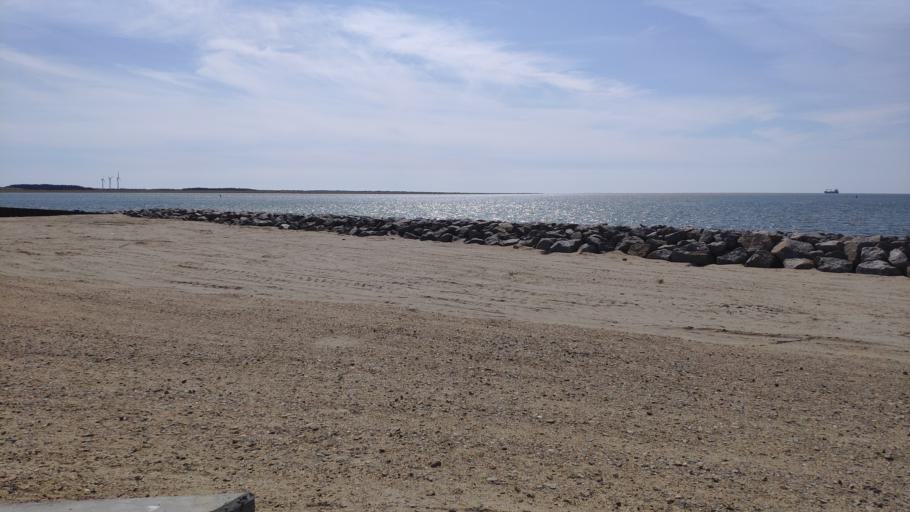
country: DK
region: South Denmark
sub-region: Fano Kommune
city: Nordby
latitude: 55.4820
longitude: 8.4077
